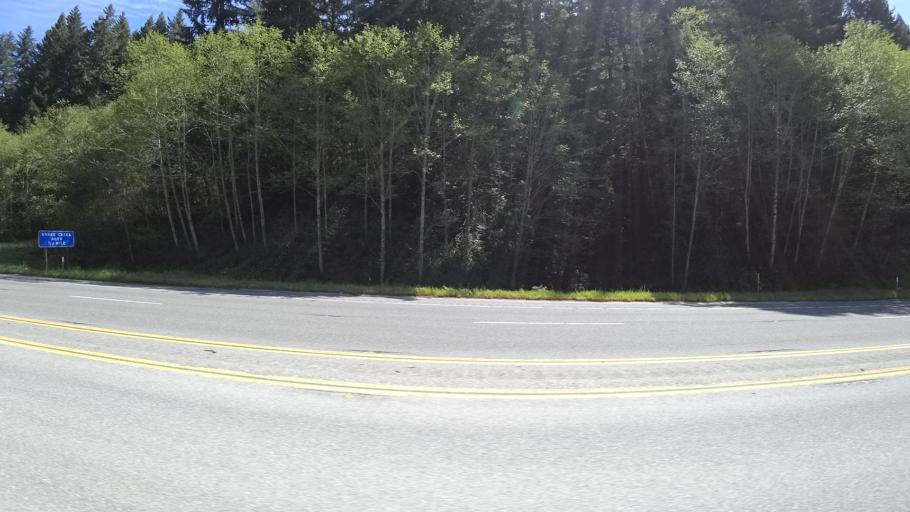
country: US
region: California
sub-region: Humboldt County
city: Westhaven-Moonstone
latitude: 41.3811
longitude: -123.9950
